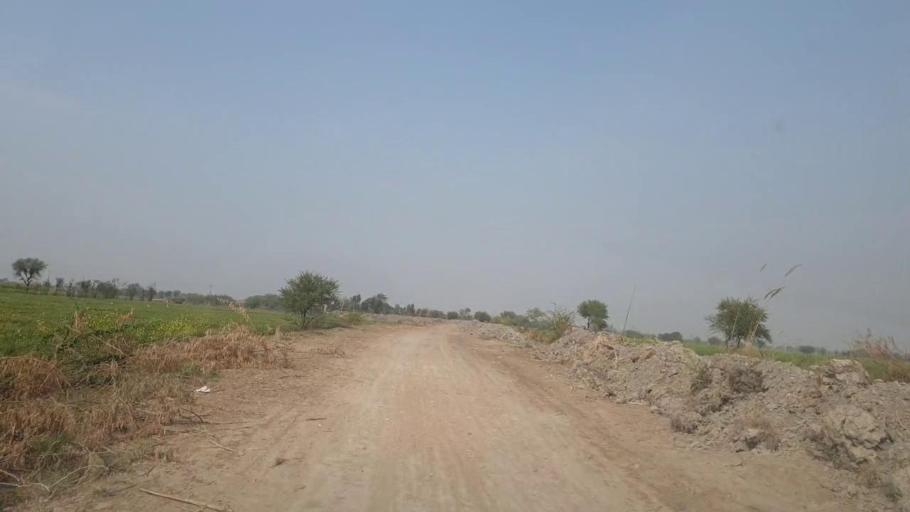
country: PK
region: Sindh
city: Mirpur Khas
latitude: 25.5652
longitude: 69.1432
